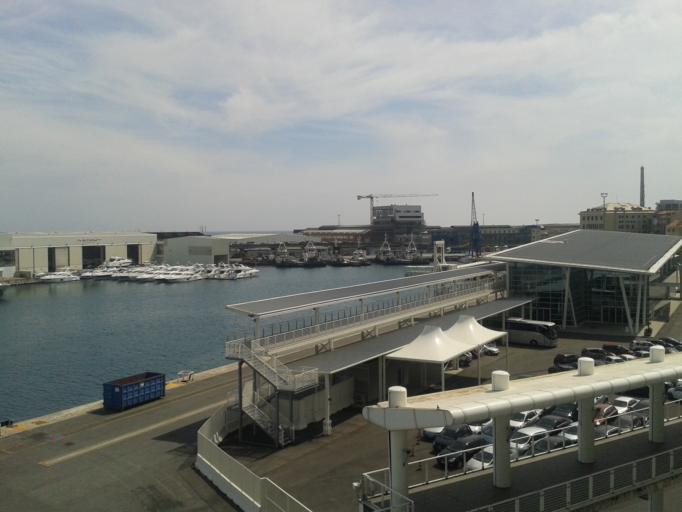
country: IT
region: Liguria
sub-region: Provincia di Savona
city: Savona
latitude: 44.3116
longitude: 8.4895
